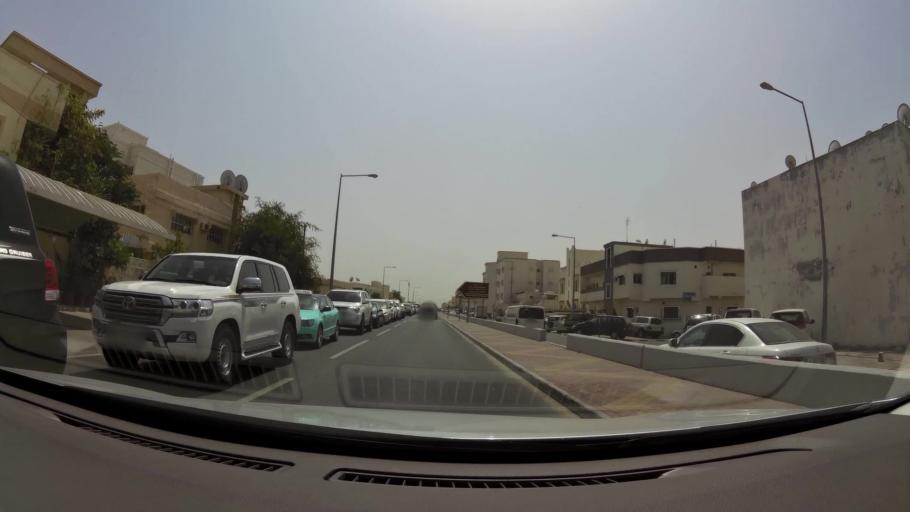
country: QA
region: Baladiyat ar Rayyan
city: Ar Rayyan
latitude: 25.3209
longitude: 51.4766
